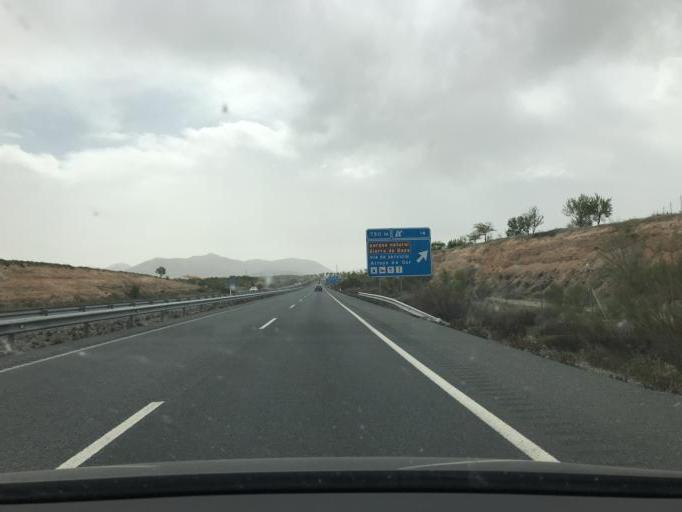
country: ES
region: Andalusia
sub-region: Provincia de Granada
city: Gor
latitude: 37.3925
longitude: -3.0208
